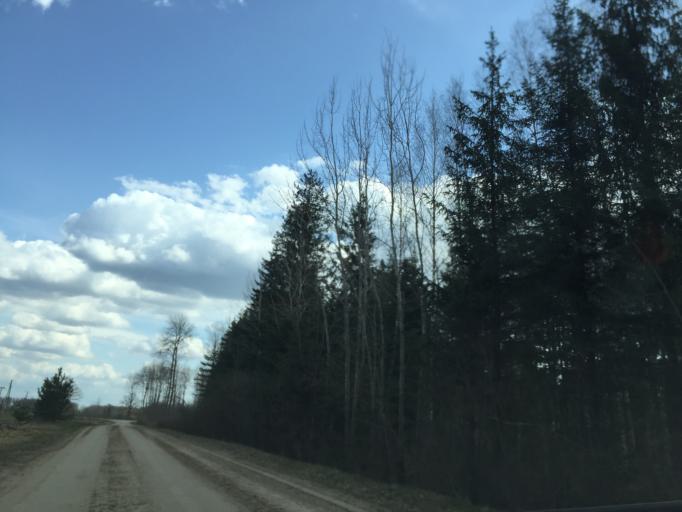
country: LV
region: Skriveri
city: Skriveri
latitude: 56.7566
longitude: 25.1657
